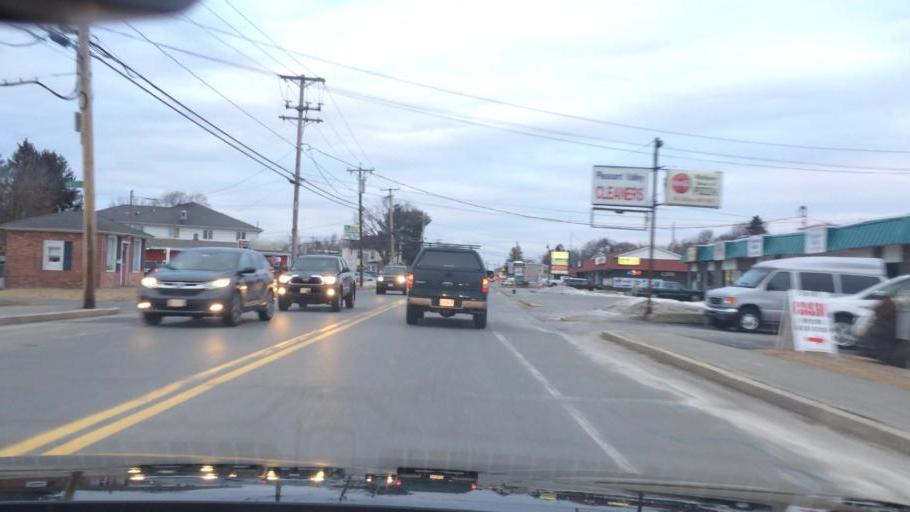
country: US
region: Massachusetts
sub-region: Essex County
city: North Andover
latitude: 42.7410
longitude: -71.1317
